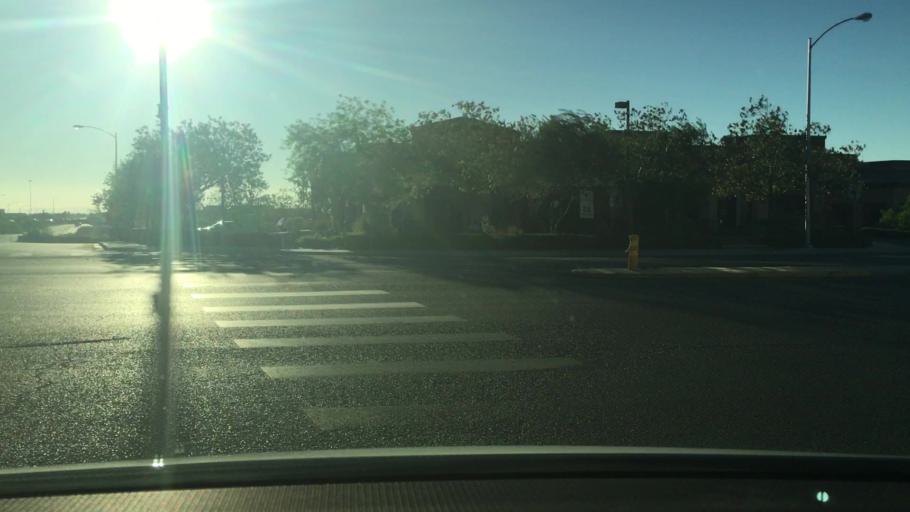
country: US
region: Nevada
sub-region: Clark County
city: Summerlin South
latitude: 36.0776
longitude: -115.2978
